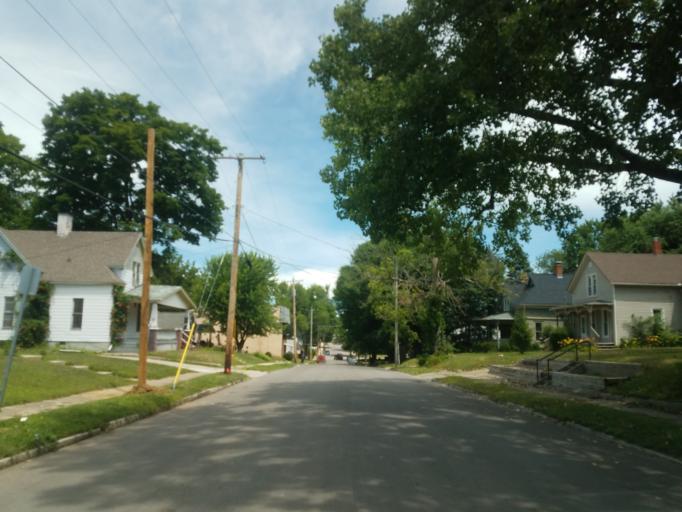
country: US
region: Illinois
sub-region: McLean County
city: Bloomington
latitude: 40.4723
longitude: -88.9856
